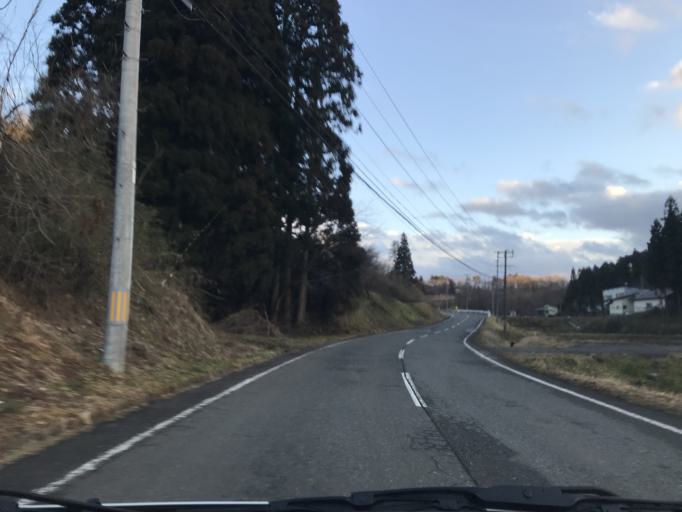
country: JP
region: Iwate
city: Ichinoseki
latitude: 38.9623
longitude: 141.0923
